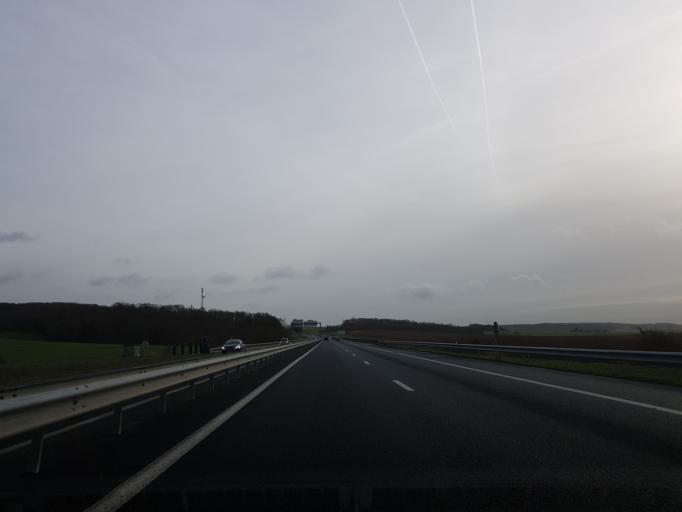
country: FR
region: Bourgogne
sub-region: Departement de l'Yonne
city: Soucy
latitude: 48.2655
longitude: 3.3022
